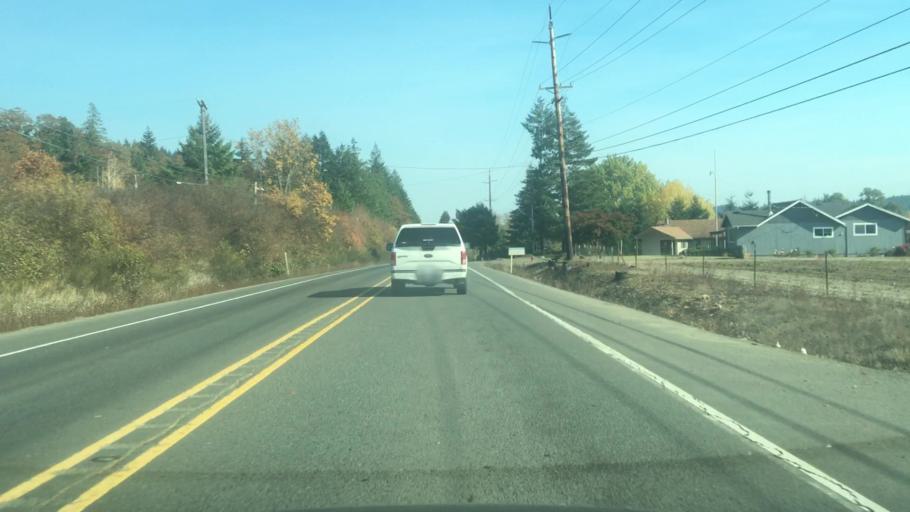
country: US
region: Oregon
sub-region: Polk County
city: Grand Ronde
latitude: 45.0583
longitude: -123.6005
